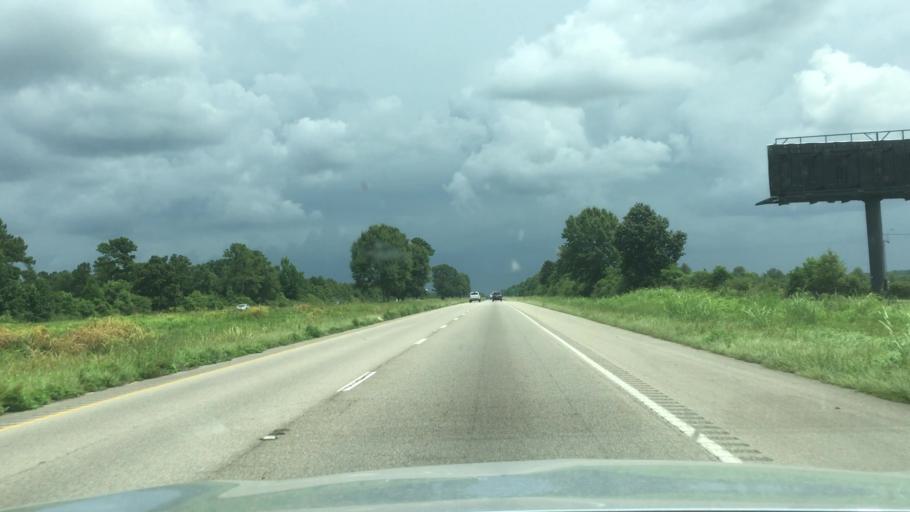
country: US
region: Mississippi
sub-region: Pearl River County
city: Carriere
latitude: 30.5798
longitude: -89.6294
